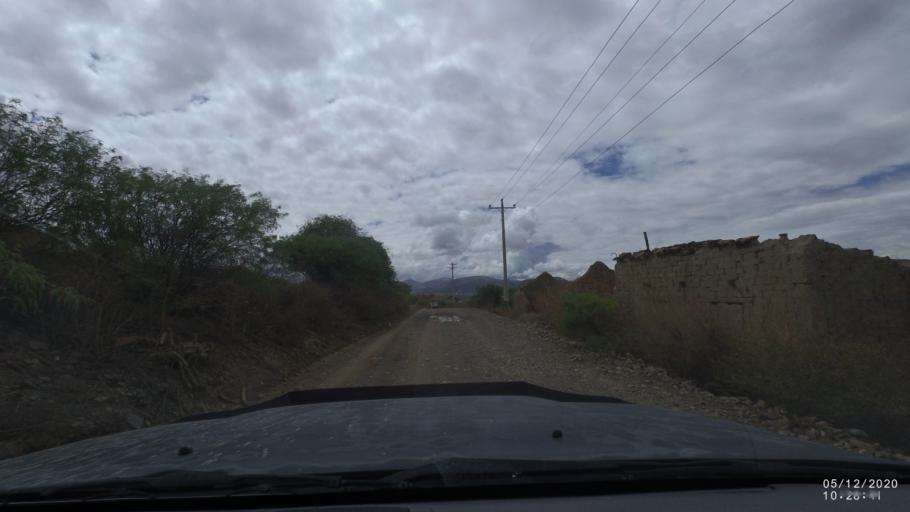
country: BO
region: Cochabamba
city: Sipe Sipe
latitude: -17.5391
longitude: -66.2717
